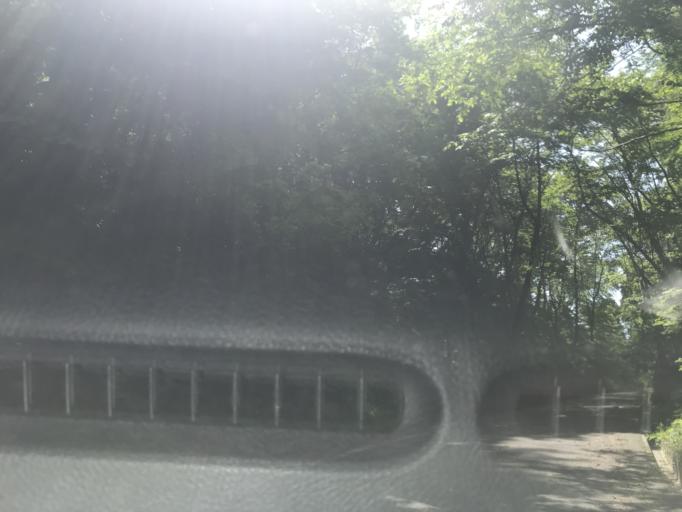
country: JP
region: Iwate
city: Ichinoseki
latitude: 38.9558
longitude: 141.2436
